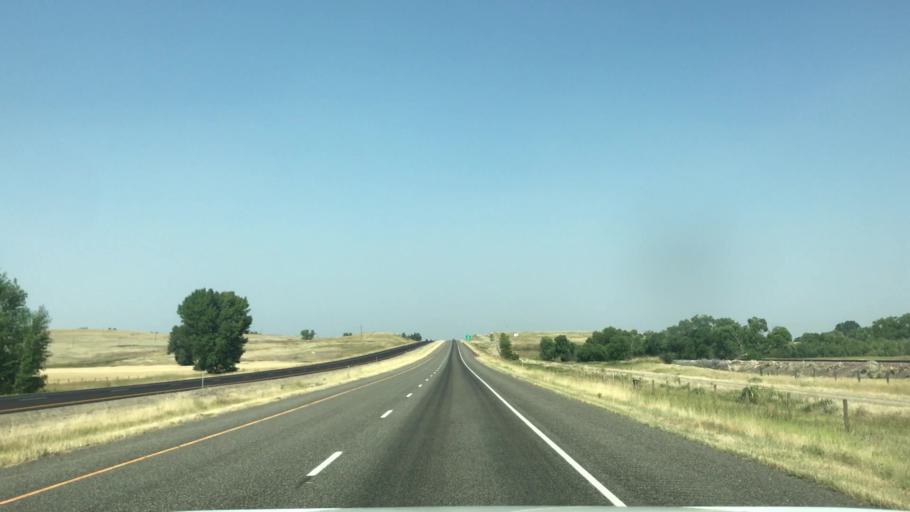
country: US
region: Montana
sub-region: Cascade County
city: Sun Prairie
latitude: 47.2426
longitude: -111.7258
